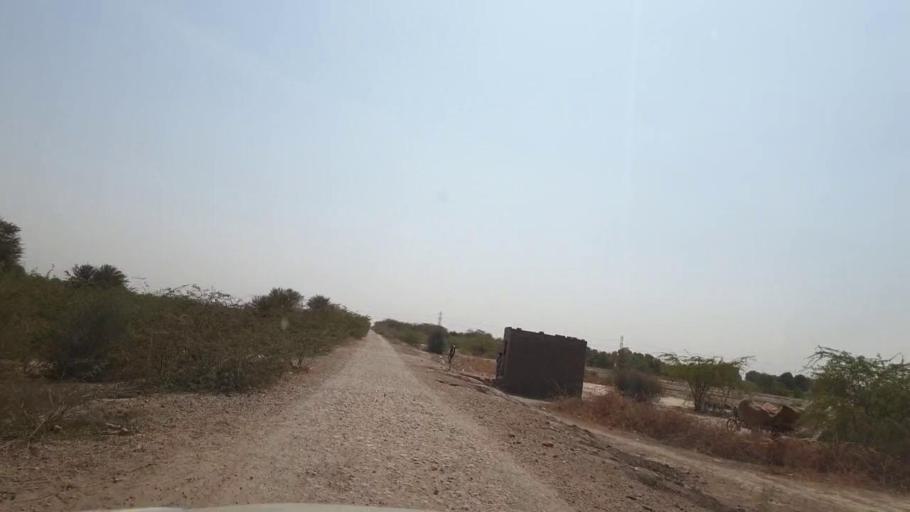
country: PK
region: Sindh
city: Nabisar
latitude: 25.0641
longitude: 69.5526
